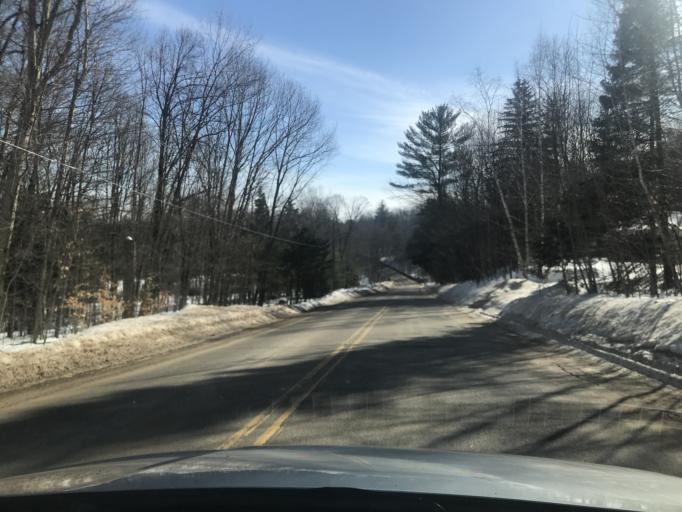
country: US
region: Michigan
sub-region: Dickinson County
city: Kingsford
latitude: 45.4040
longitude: -88.3464
